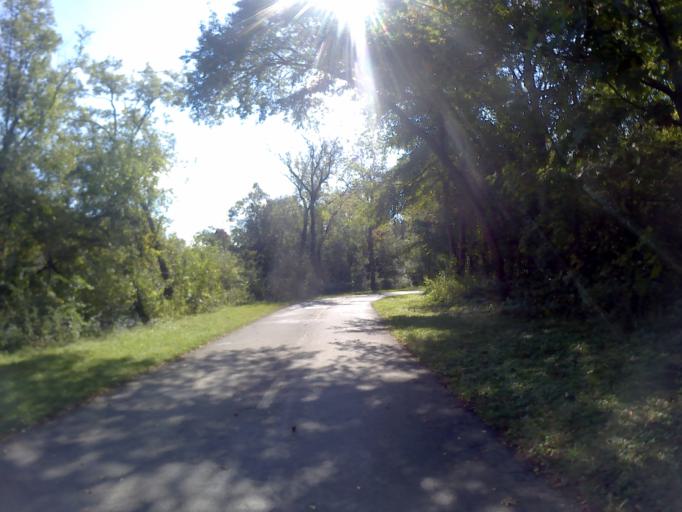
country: US
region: Illinois
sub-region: DuPage County
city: Naperville
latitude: 41.7419
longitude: -88.1275
